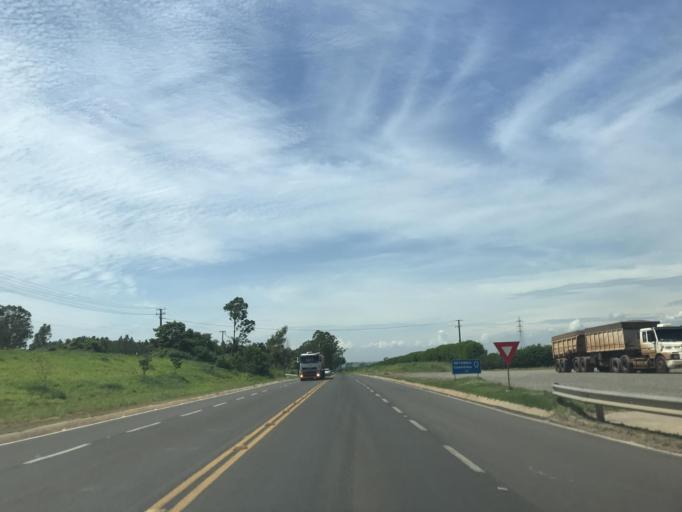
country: BR
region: Parana
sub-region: Paranavai
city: Nova Aurora
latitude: -22.9840
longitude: -52.6017
